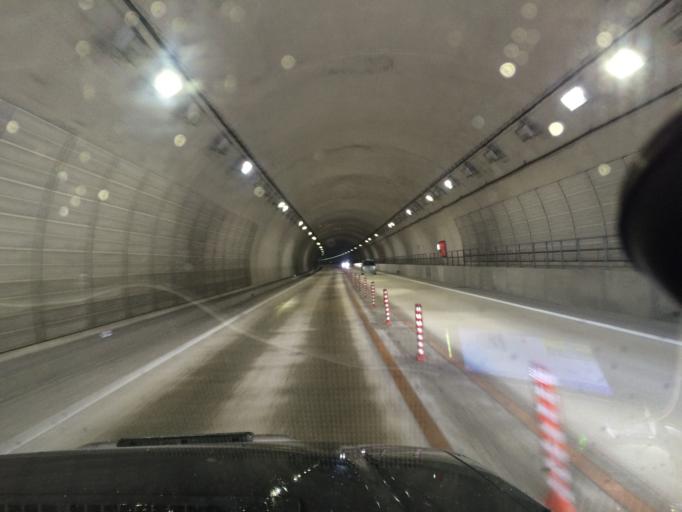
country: JP
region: Hyogo
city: Toyooka
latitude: 35.4637
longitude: 134.7638
